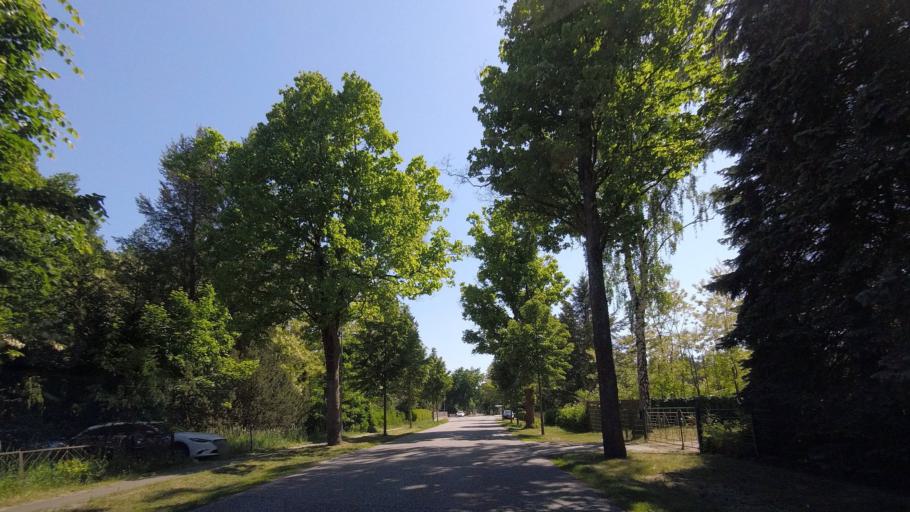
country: DE
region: Brandenburg
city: Gross Kreutz
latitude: 52.3573
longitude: 12.7657
